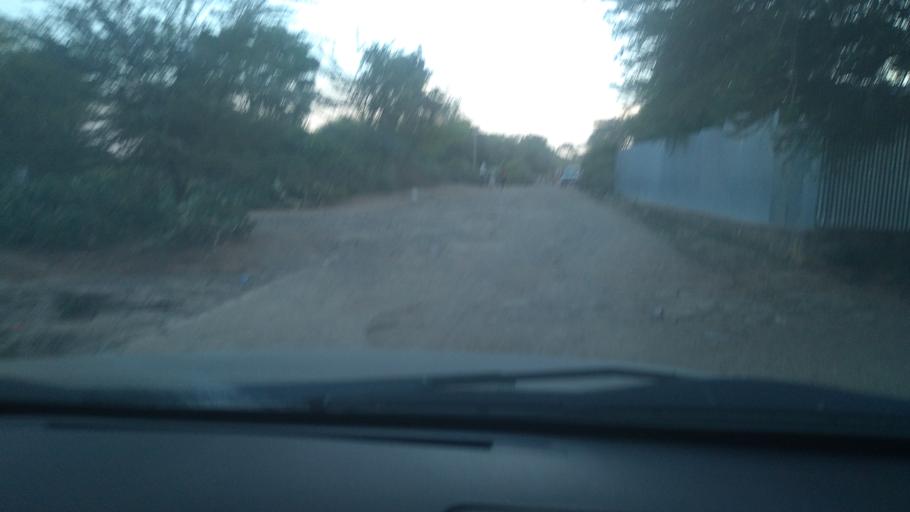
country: ET
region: Oromiya
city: Asbe Teferi
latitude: 9.2370
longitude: 40.7602
